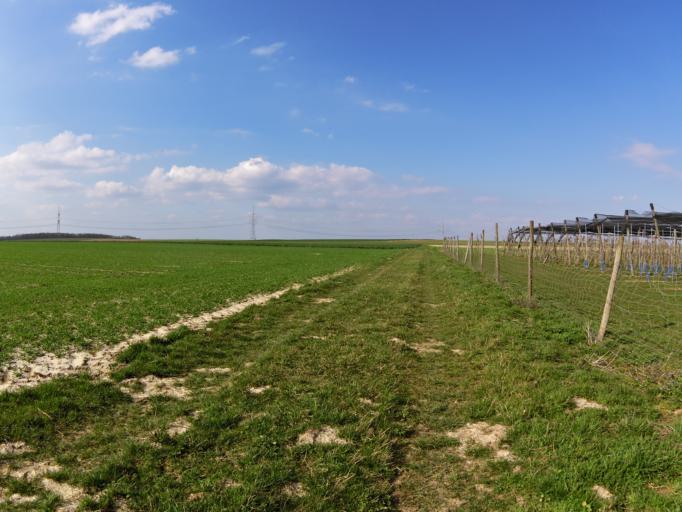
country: DE
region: Bavaria
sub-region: Regierungsbezirk Unterfranken
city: Biebelried
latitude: 49.7951
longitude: 10.0739
